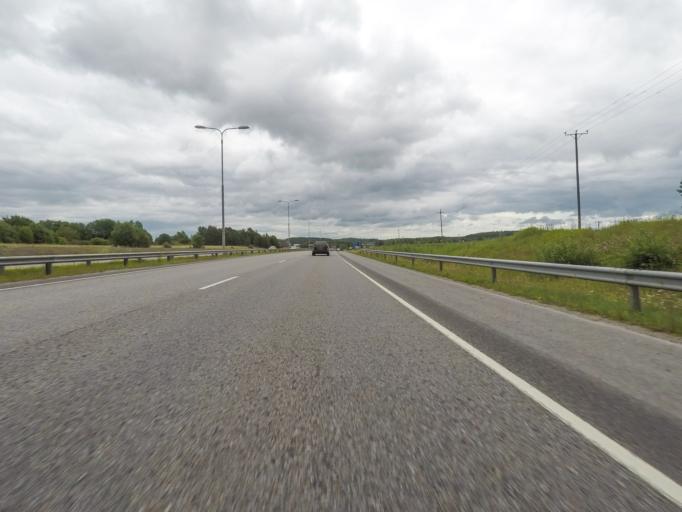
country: FI
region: Varsinais-Suomi
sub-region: Turku
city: Turku
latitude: 60.4939
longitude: 22.3083
